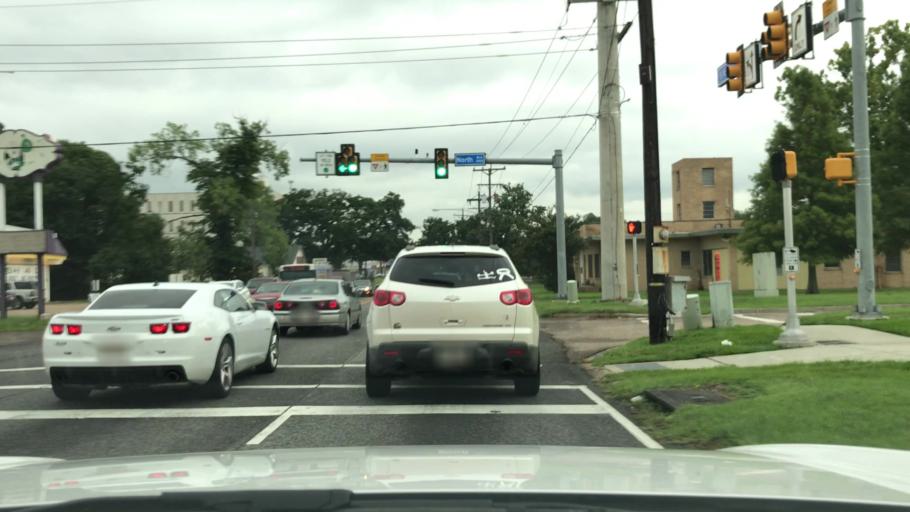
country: US
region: Louisiana
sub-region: East Baton Rouge Parish
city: Baton Rouge
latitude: 30.4485
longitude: -91.1388
